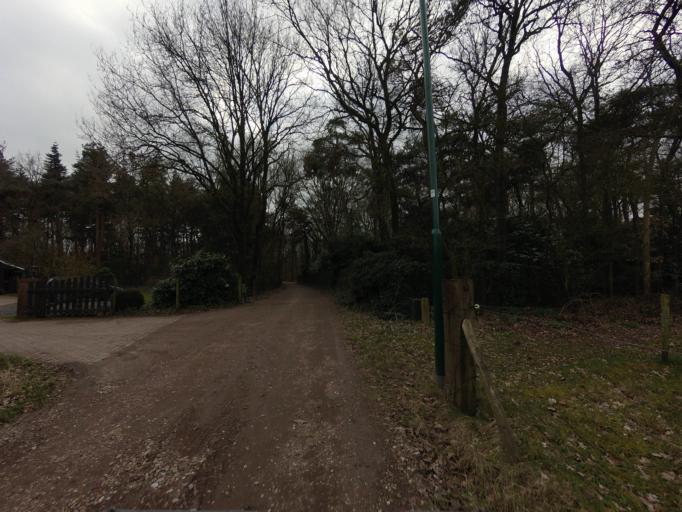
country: NL
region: North Holland
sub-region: Gemeente Laren
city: Laren
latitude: 52.2286
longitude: 5.2267
